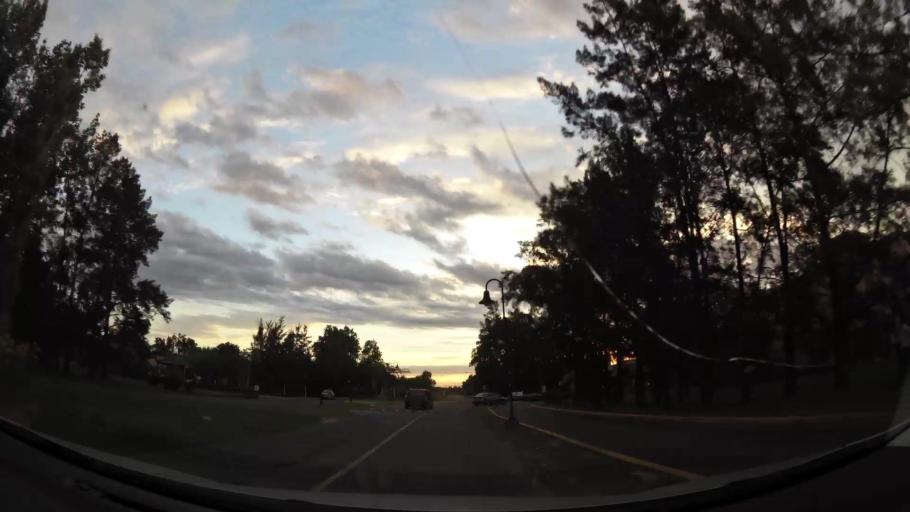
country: AR
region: Buenos Aires
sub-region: Partido de Tigre
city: Tigre
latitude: -34.4405
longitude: -58.6488
